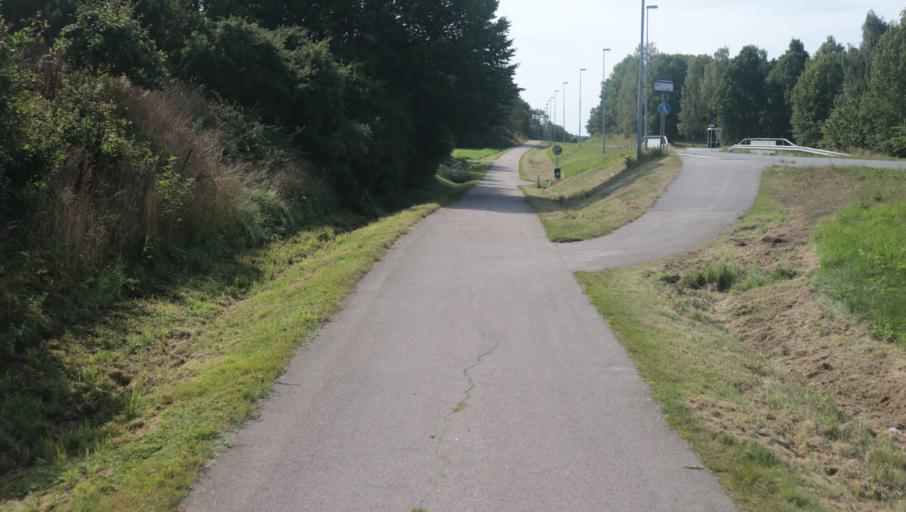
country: SE
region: Blekinge
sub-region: Karlshamns Kommun
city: Karlshamn
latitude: 56.2067
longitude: 14.8517
